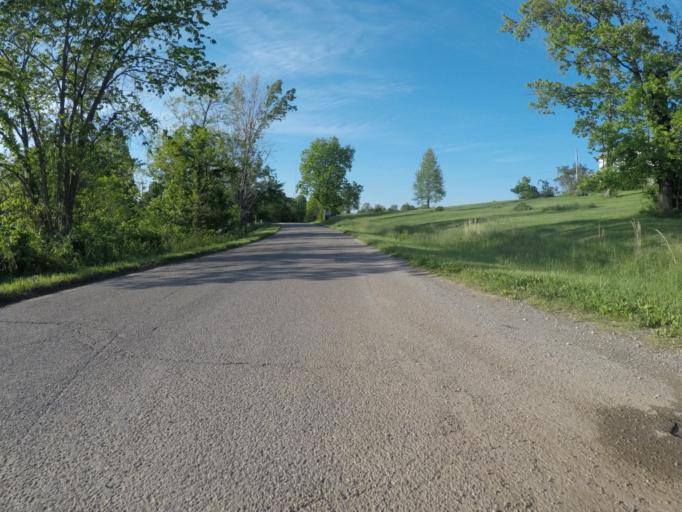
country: US
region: West Virginia
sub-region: Cabell County
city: Huntington
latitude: 38.5066
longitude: -82.4269
